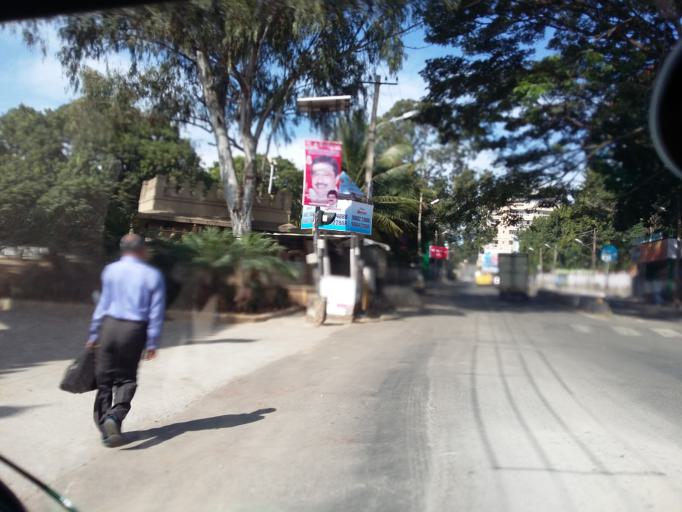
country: IN
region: Karnataka
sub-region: Bangalore Urban
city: Bangalore
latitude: 12.9954
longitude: 77.6020
